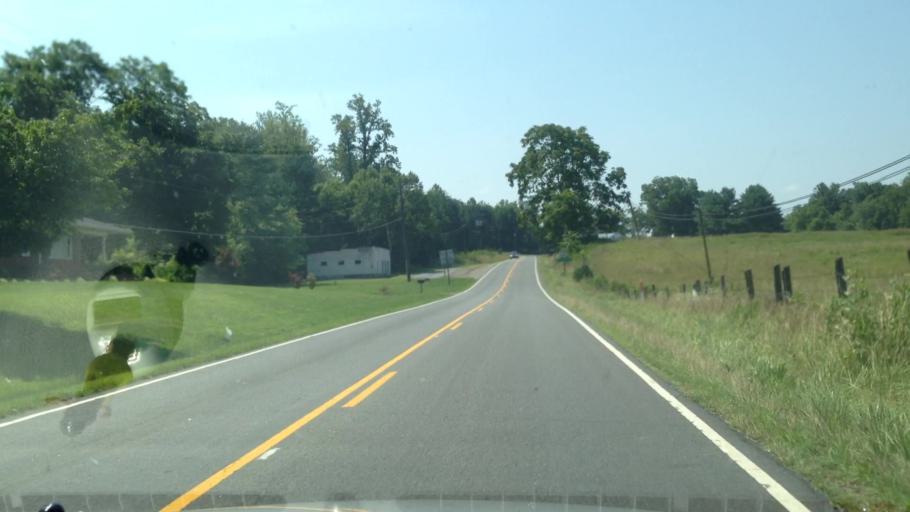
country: US
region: Virginia
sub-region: Patrick County
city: Stuart
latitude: 36.5879
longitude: -80.2800
